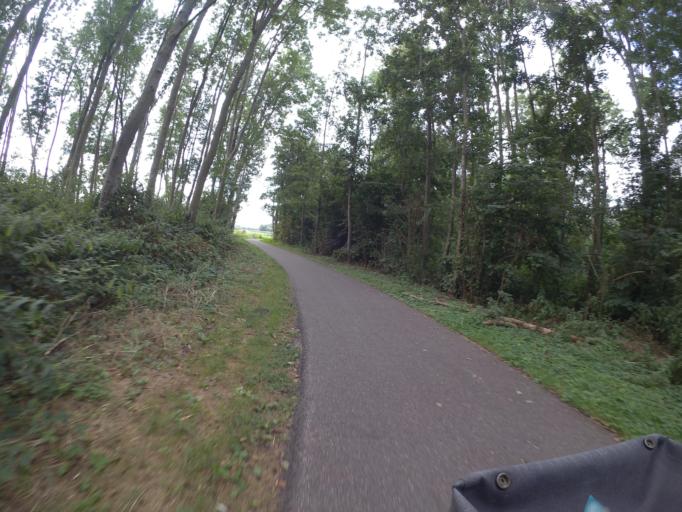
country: NL
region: North Brabant
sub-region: Roosendaal
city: Roosendaal
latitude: 51.5079
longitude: 4.4524
